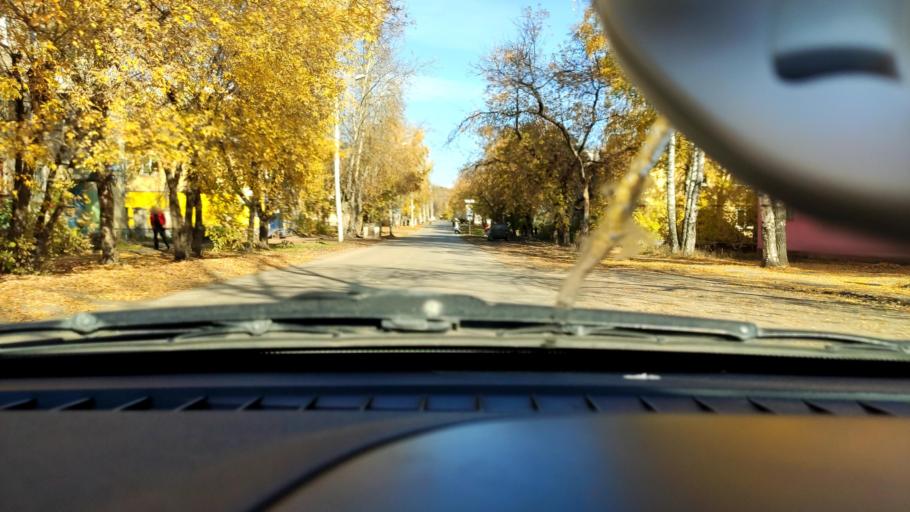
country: RU
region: Perm
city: Kondratovo
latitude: 58.0395
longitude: 56.1075
